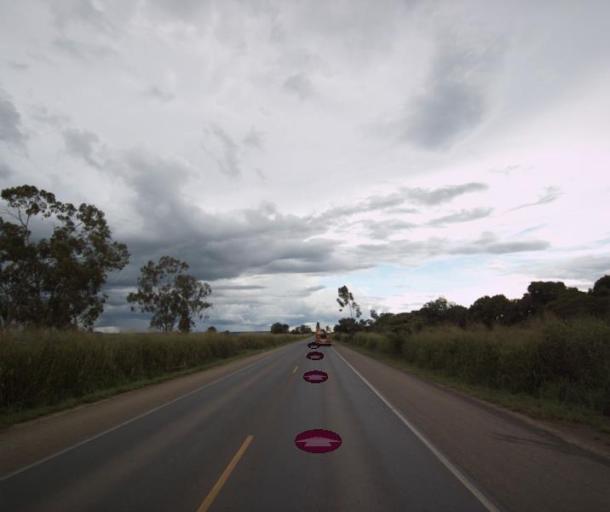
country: BR
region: Goias
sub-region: Itapaci
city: Itapaci
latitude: -15.0166
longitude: -49.4221
